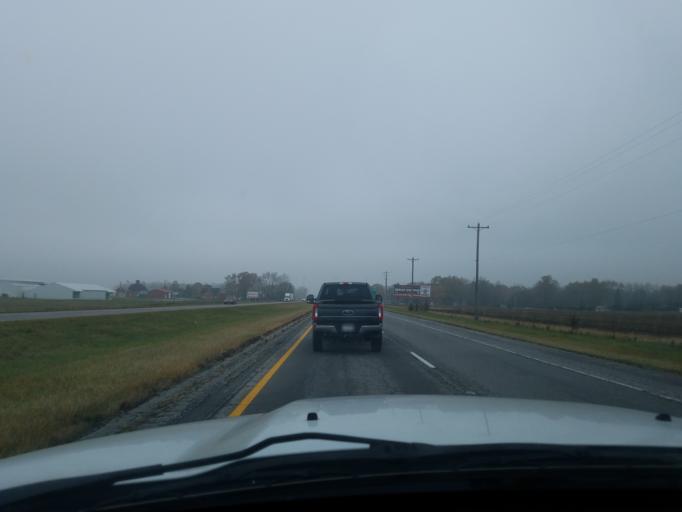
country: US
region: Indiana
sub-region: Howard County
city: Indian Heights
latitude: 40.3820
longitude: -86.1269
